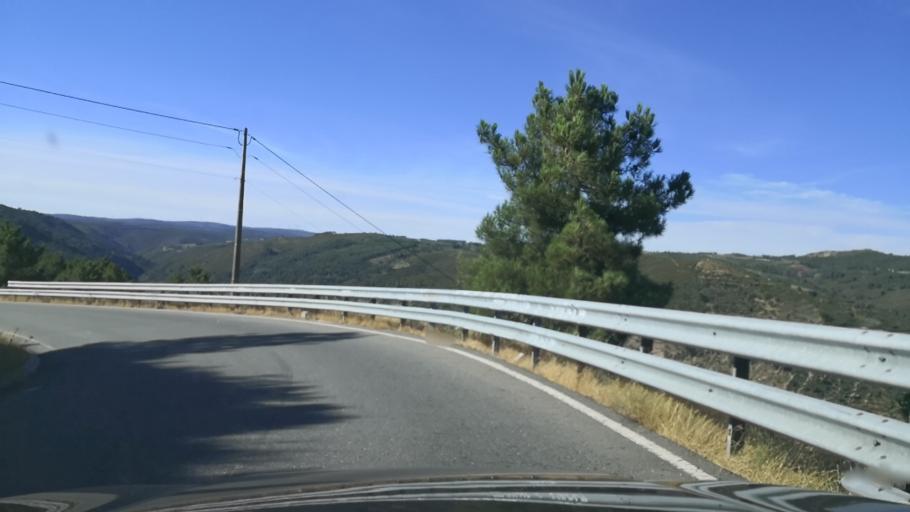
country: PT
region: Vila Real
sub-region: Murca
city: Murca
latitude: 41.4051
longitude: -7.4765
